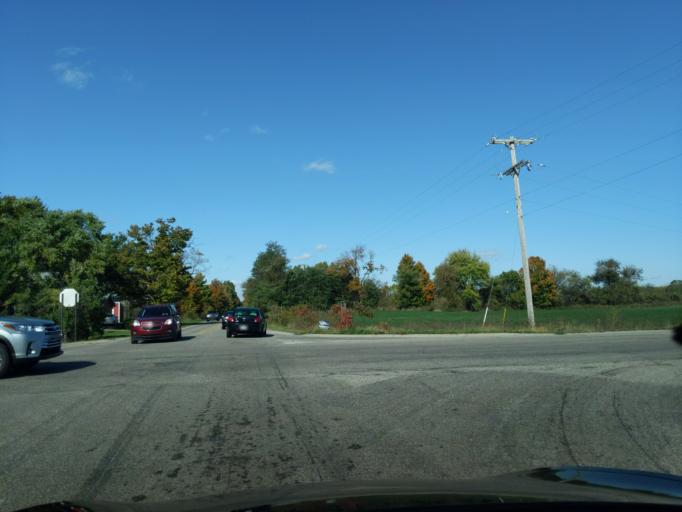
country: US
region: Michigan
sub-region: Eaton County
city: Potterville
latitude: 42.6258
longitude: -84.7977
